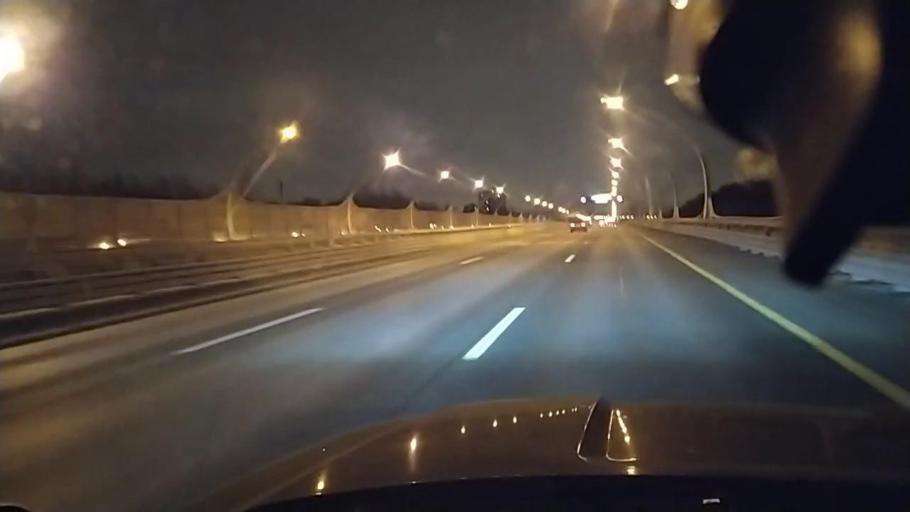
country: RU
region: Leningrad
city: Untolovo
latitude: 60.0286
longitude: 30.2012
